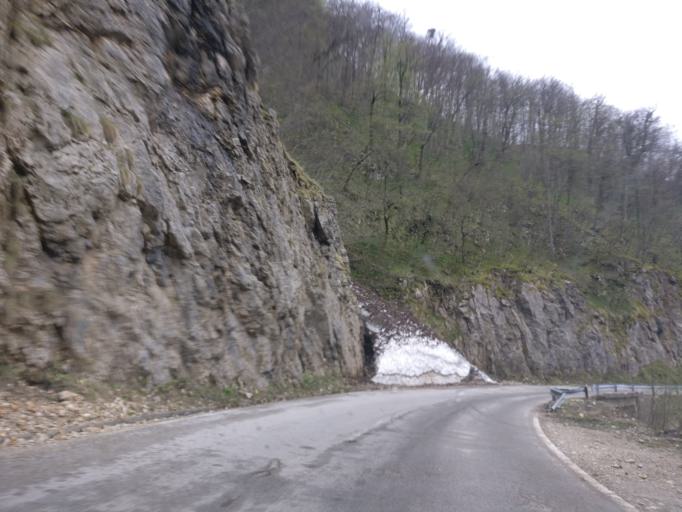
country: ME
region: Opstina Pluzine
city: Pluzine
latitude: 43.2567
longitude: 18.8431
